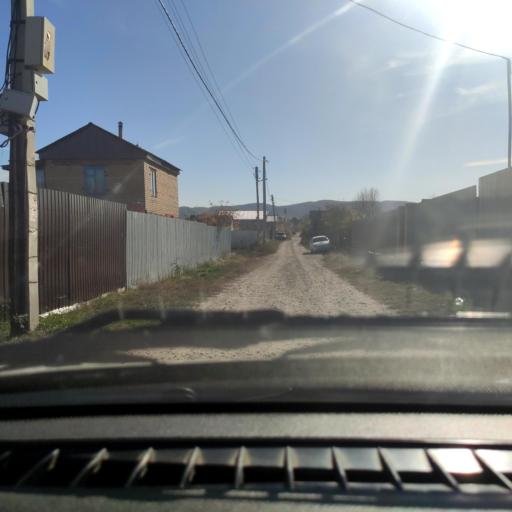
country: RU
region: Samara
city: Zhigulevsk
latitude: 53.4672
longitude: 49.5870
